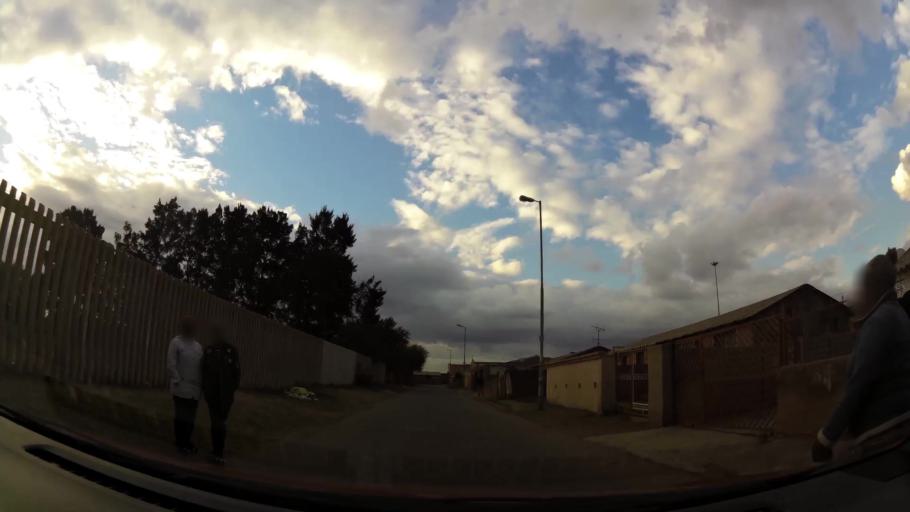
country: ZA
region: Gauteng
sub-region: City of Johannesburg Metropolitan Municipality
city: Soweto
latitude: -26.2459
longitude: 27.8278
